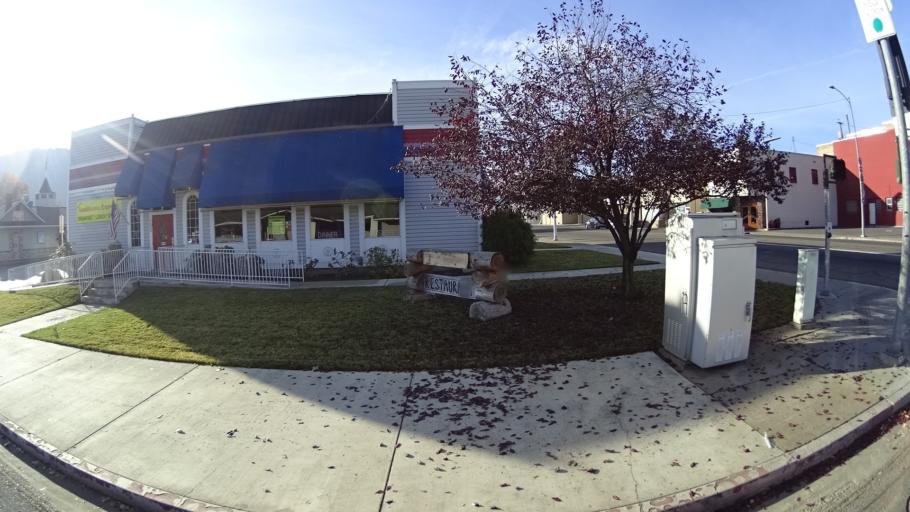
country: US
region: California
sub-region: Siskiyou County
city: Yreka
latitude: 41.7315
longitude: -122.6354
